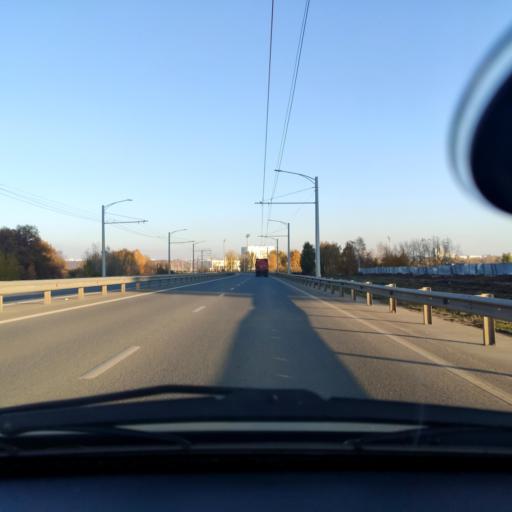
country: RU
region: Bashkortostan
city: Mikhaylovka
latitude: 54.7719
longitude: 55.9017
